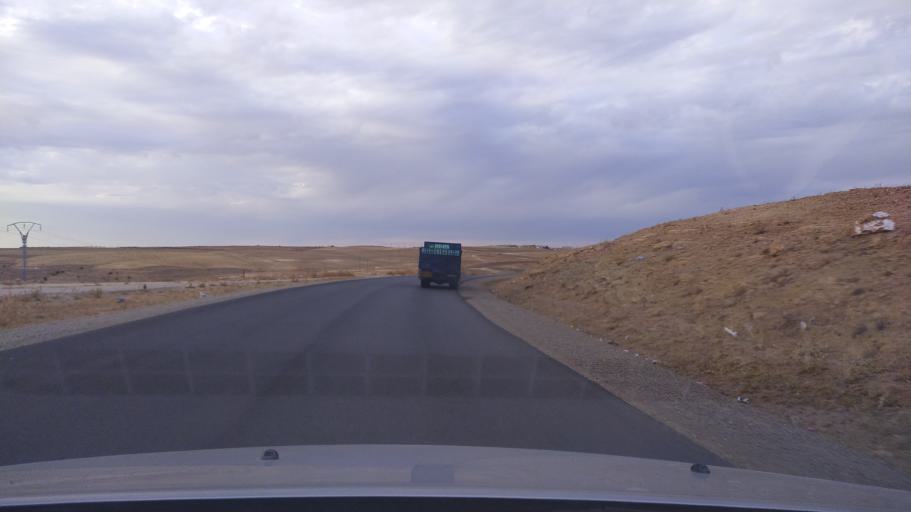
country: DZ
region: Tiaret
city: Frenda
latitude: 34.9939
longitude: 1.1286
